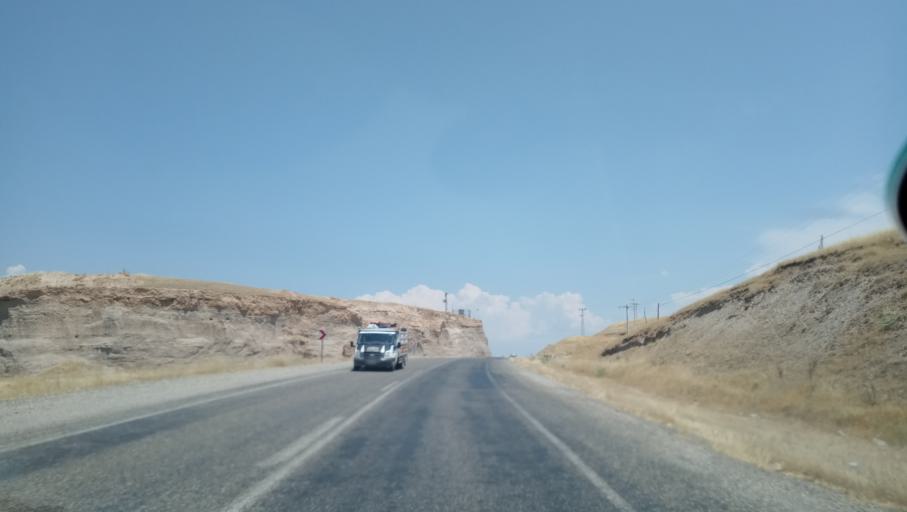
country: TR
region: Diyarbakir
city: Aralik
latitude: 37.8092
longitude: 40.7209
